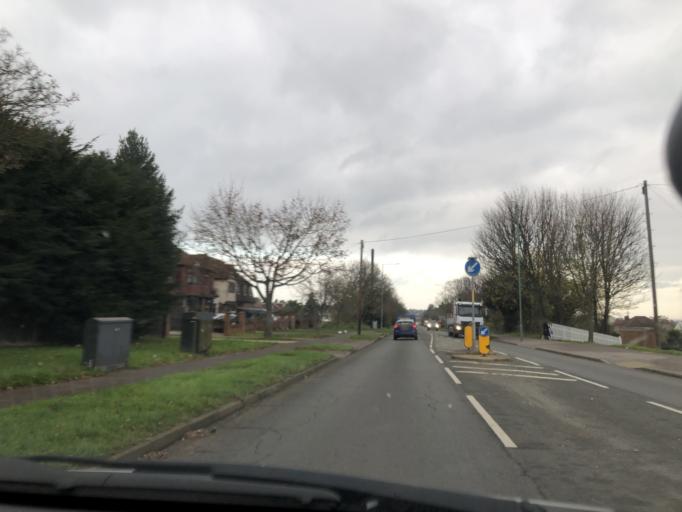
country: GB
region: England
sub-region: Kent
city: Dartford
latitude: 51.4444
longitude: 0.1934
